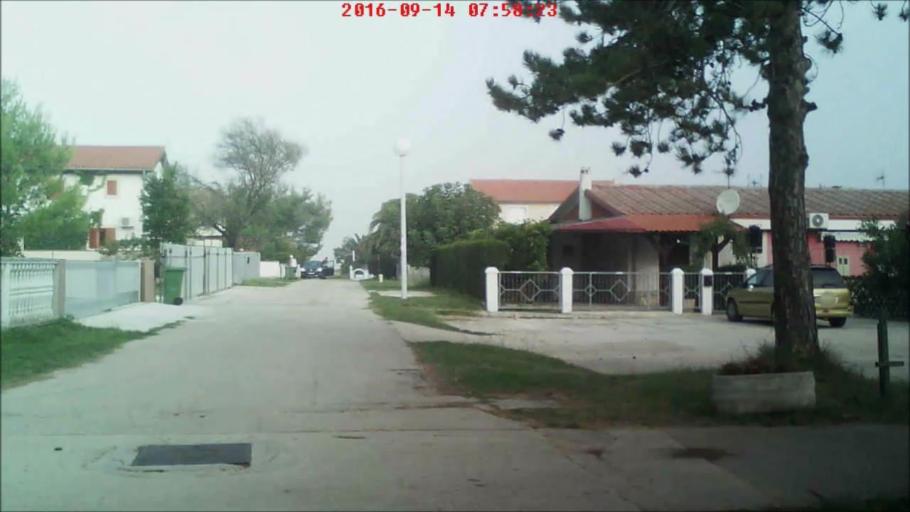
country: HR
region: Zadarska
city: Nin
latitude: 44.2595
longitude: 15.1622
